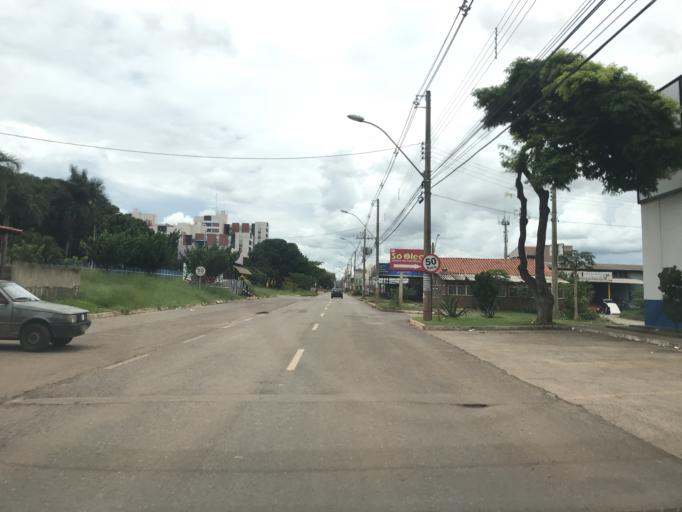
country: BR
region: Federal District
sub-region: Brasilia
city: Brasilia
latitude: -15.8205
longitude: -47.9559
